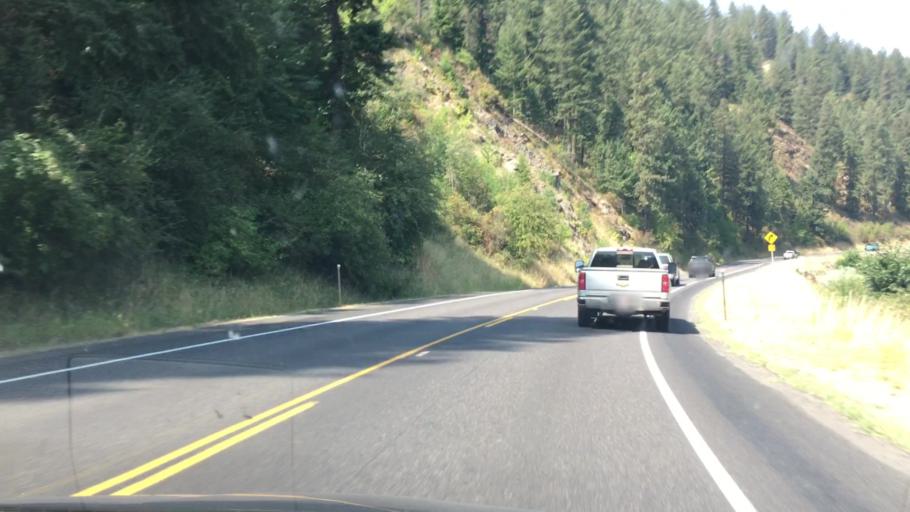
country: US
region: Idaho
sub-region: Clearwater County
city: Orofino
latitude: 46.4894
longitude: -116.4532
